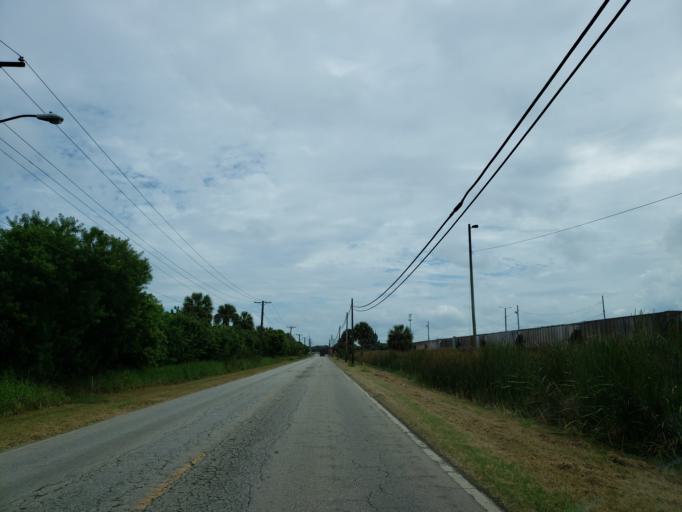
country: US
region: Florida
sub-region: Hillsborough County
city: Palm River-Clair Mel
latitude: 27.9063
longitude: -82.4074
